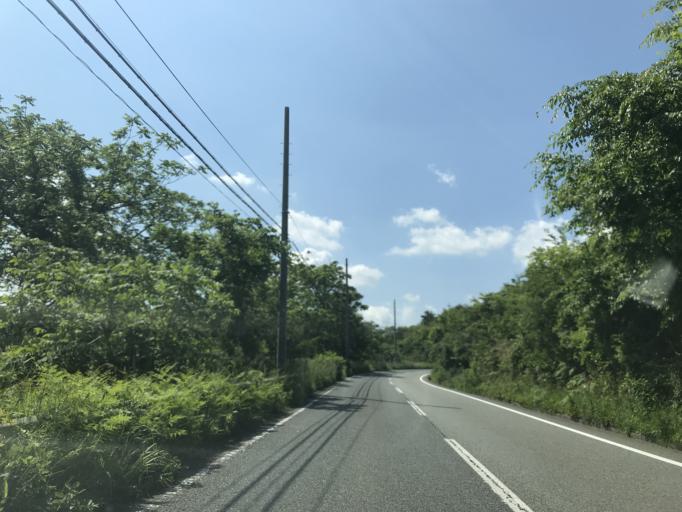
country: JP
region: Miyagi
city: Furukawa
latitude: 38.7195
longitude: 140.9486
